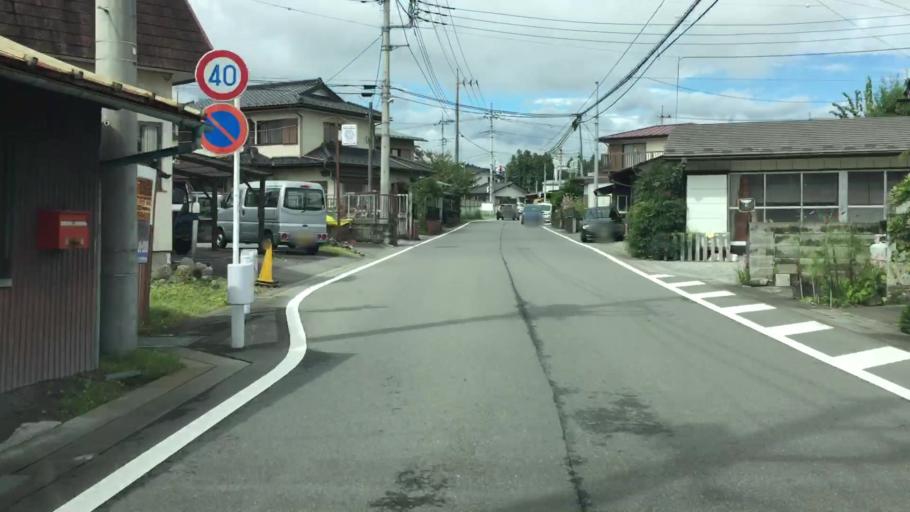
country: JP
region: Tochigi
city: Imaichi
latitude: 36.7358
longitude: 139.6863
